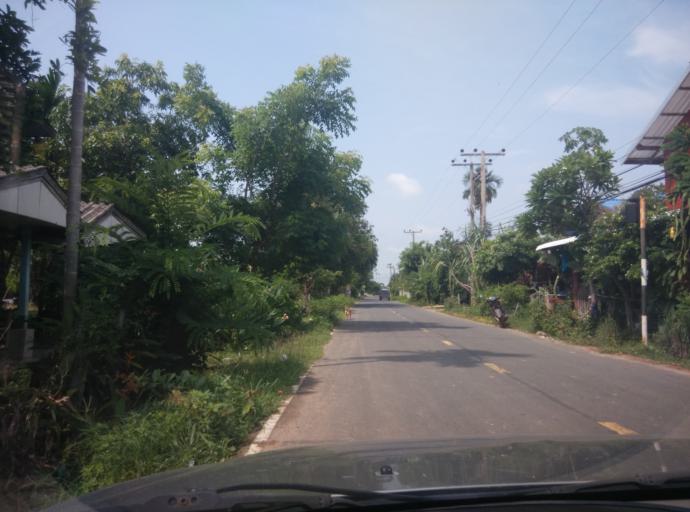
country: TH
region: Sisaket
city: Huai Thap Than
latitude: 14.9840
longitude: 104.0709
